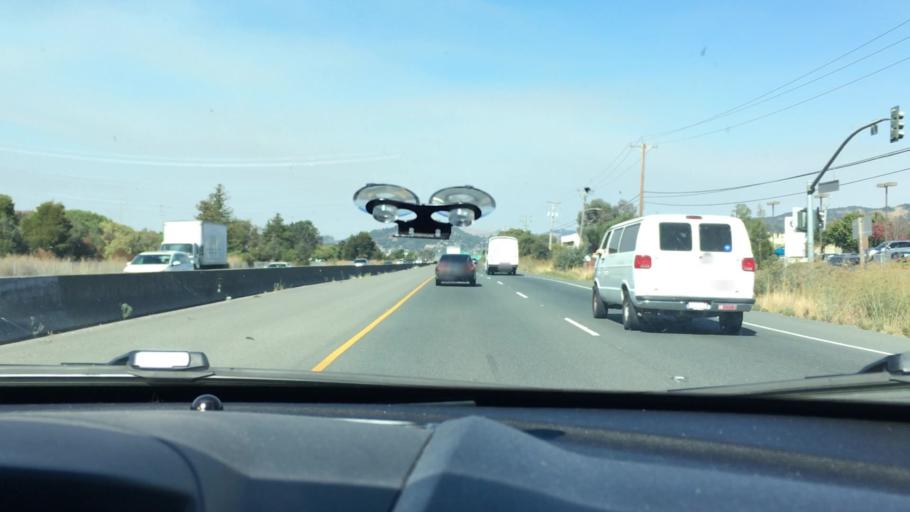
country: US
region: California
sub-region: Marin County
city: Corte Madera
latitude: 37.9503
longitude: -122.4950
